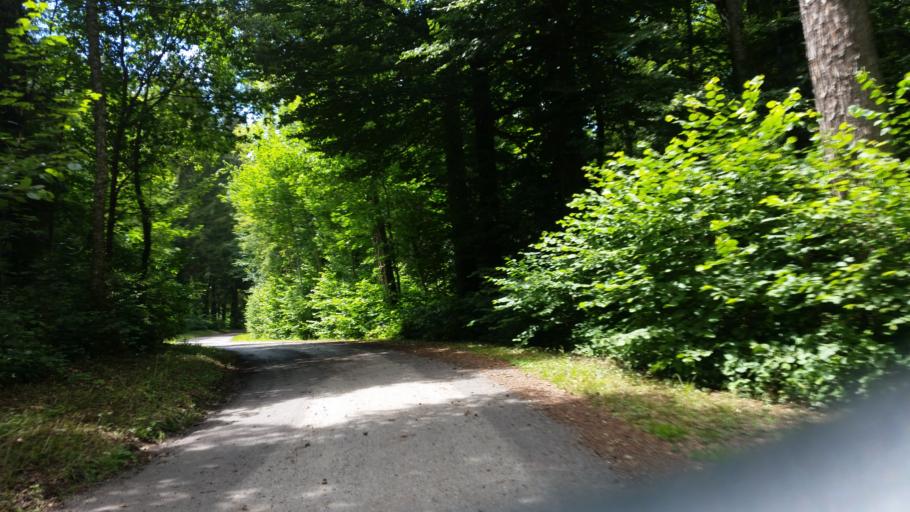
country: CH
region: Vaud
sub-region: Lausanne District
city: Cheseaux
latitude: 46.6101
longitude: 6.6000
